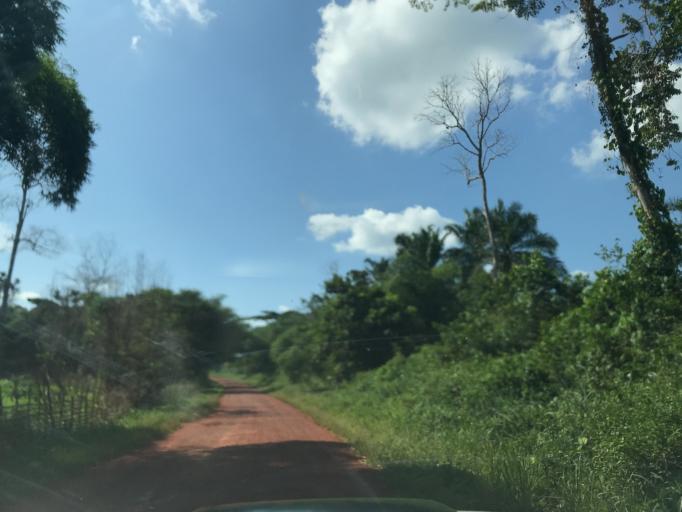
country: CD
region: Eastern Province
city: Kisangani
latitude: 1.2229
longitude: 25.2688
